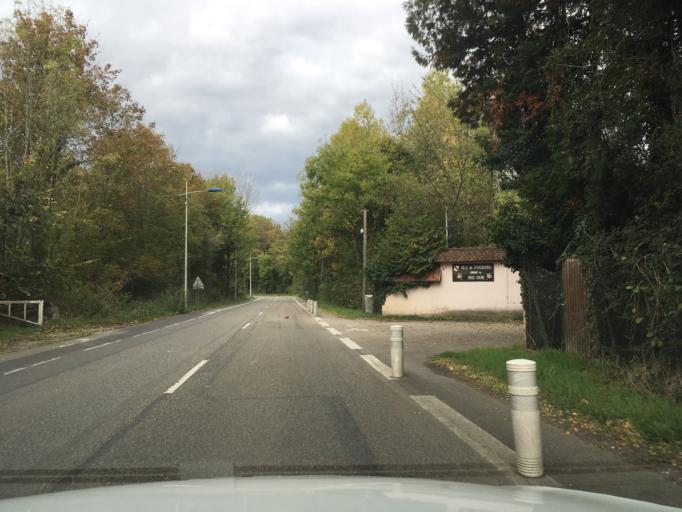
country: DE
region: Baden-Wuerttemberg
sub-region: Freiburg Region
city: Kehl
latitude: 48.5275
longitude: 7.7761
